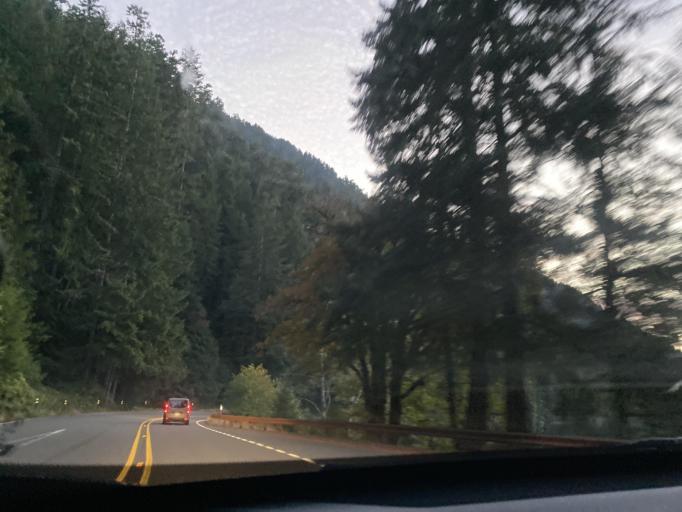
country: CA
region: British Columbia
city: Sooke
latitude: 48.0494
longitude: -123.8533
